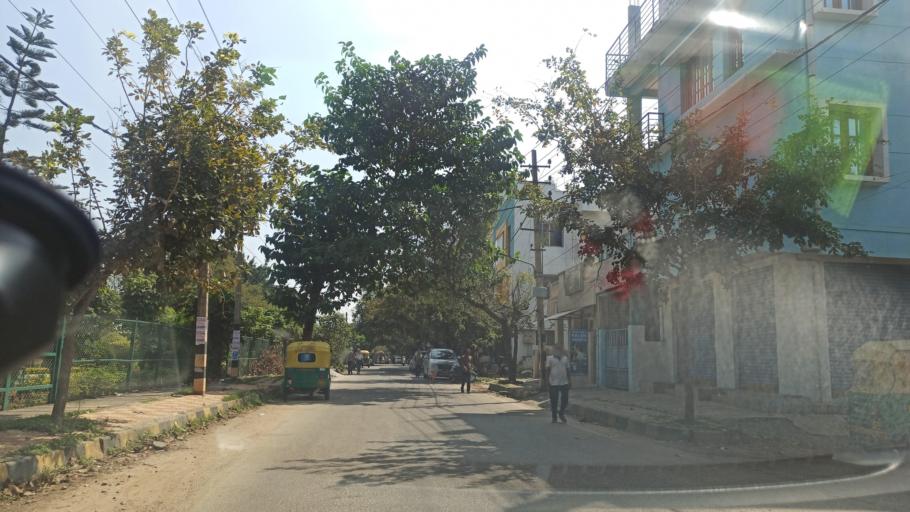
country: IN
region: Karnataka
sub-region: Bangalore Urban
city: Yelahanka
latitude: 13.0625
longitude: 77.5860
